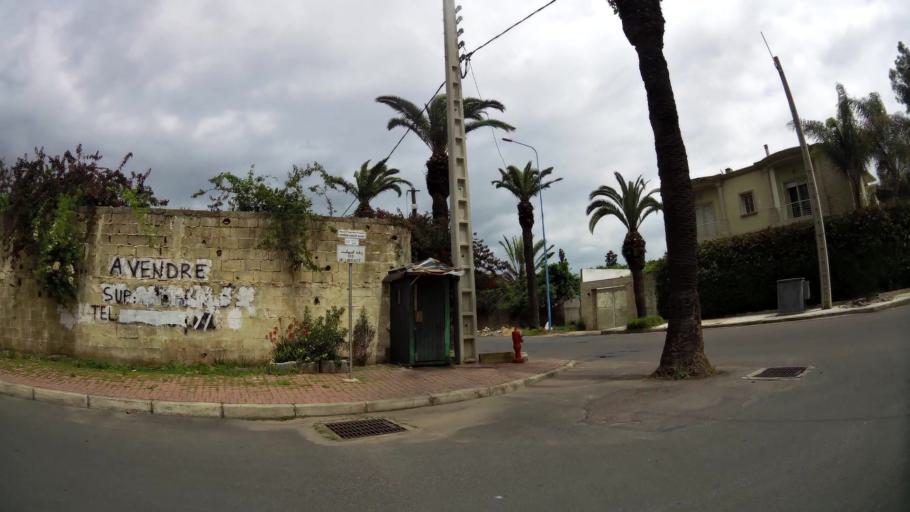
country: MA
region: Grand Casablanca
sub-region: Casablanca
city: Casablanca
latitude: 33.5571
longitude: -7.6180
